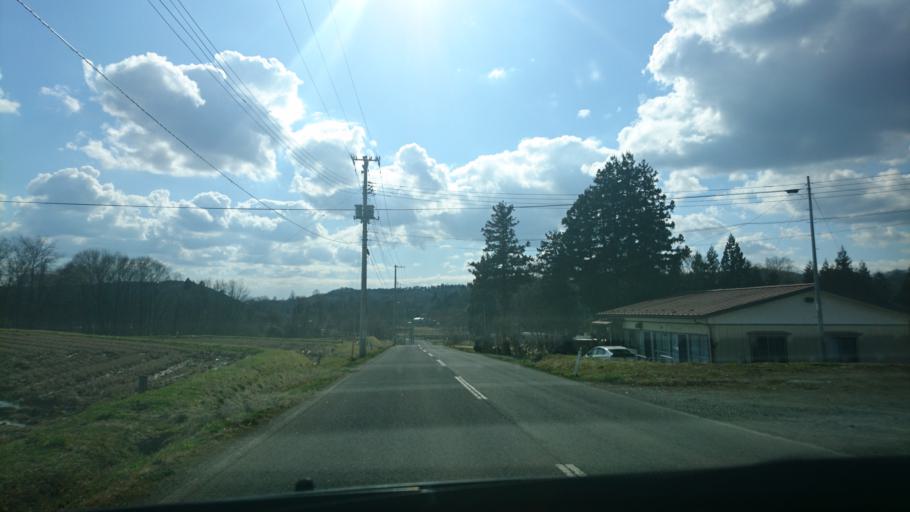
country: JP
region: Iwate
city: Kitakami
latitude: 39.2316
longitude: 141.1855
